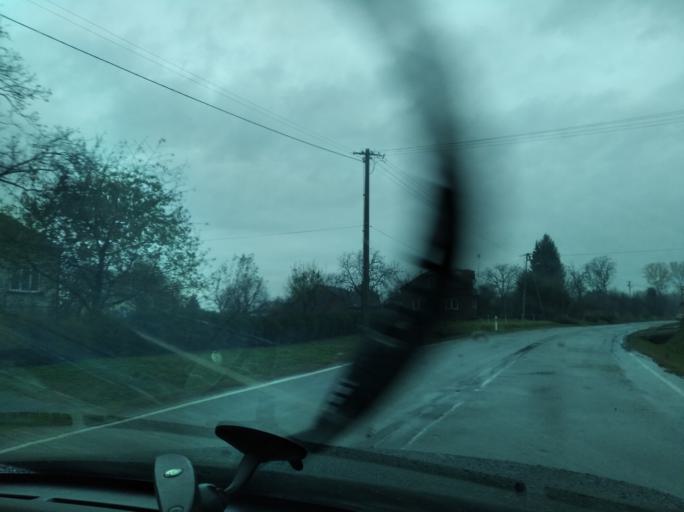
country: PL
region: Subcarpathian Voivodeship
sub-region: Powiat lancucki
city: Albigowa
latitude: 50.0064
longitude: 22.2139
